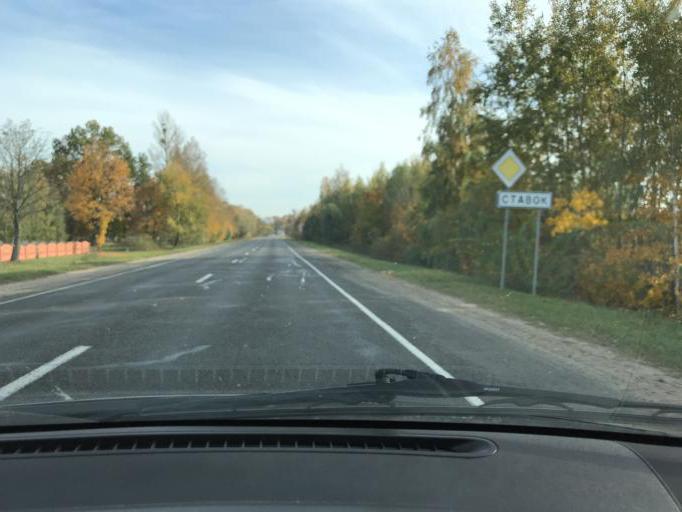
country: BY
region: Brest
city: Asnyezhytsy
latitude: 52.2010
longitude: 26.0624
